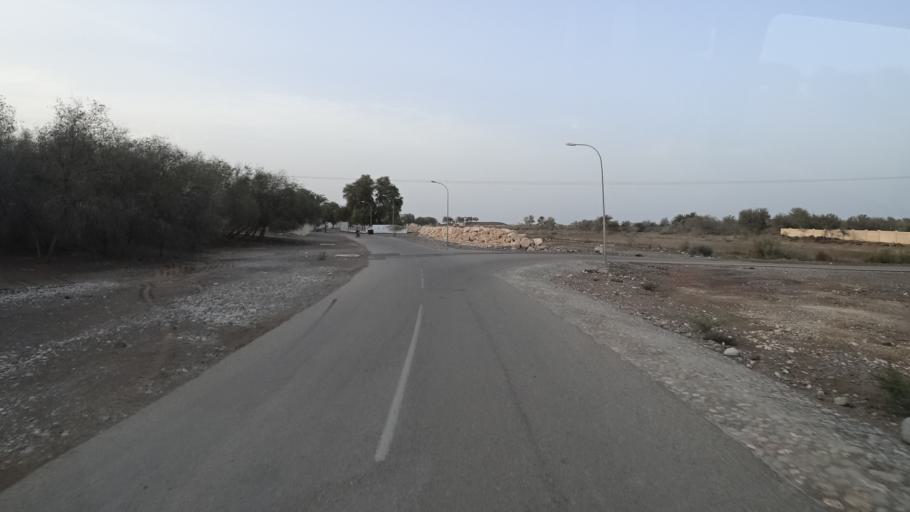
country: OM
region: Muhafazat Masqat
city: Muscat
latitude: 23.2121
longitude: 58.9738
